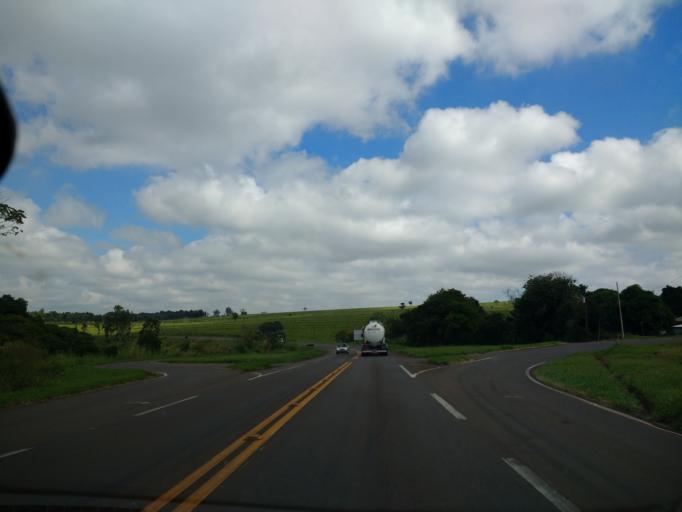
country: BR
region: Parana
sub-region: Cruzeiro Do Oeste
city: Cruzeiro do Oeste
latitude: -23.7738
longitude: -53.0211
